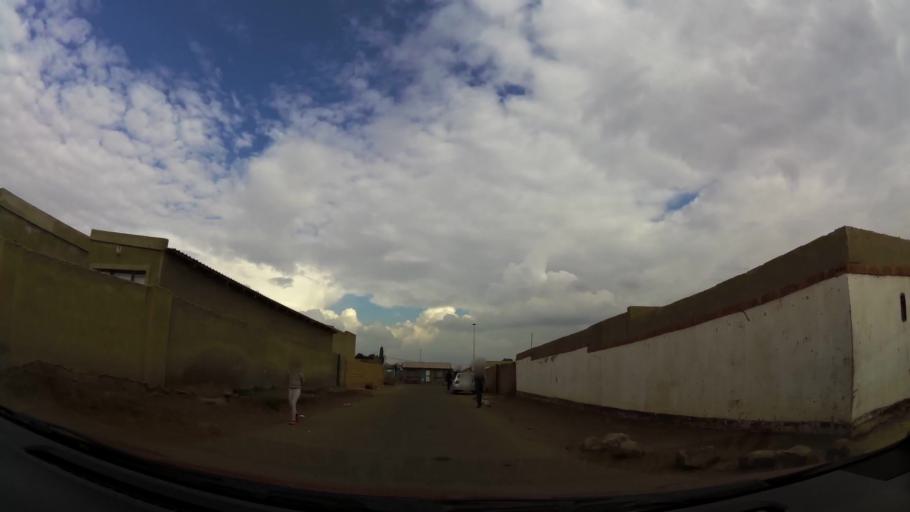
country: ZA
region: Gauteng
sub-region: City of Johannesburg Metropolitan Municipality
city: Soweto
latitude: -26.2432
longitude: 27.8537
